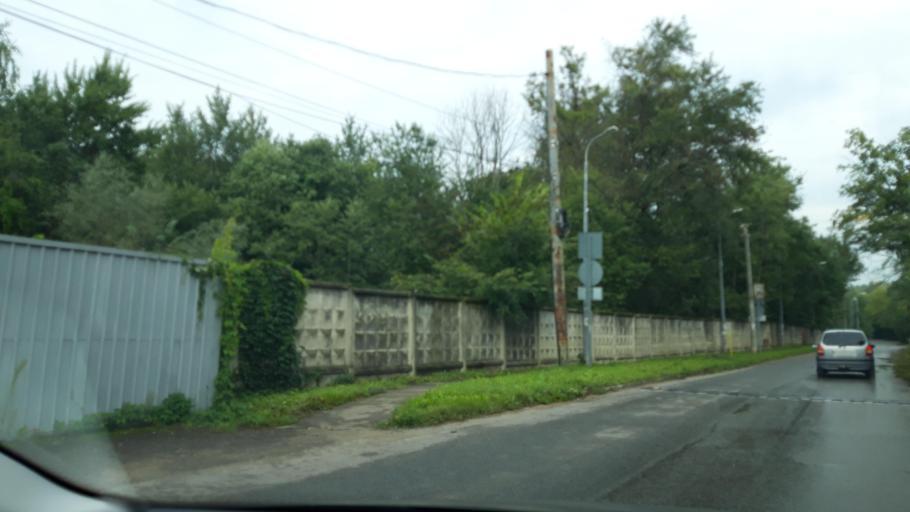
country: RU
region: Moskovskaya
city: Novopodrezkovo
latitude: 55.8836
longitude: 37.3685
